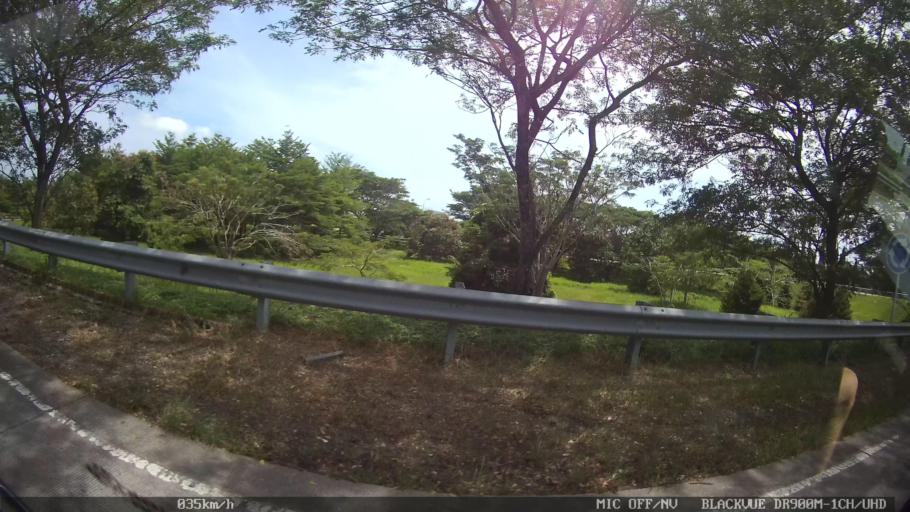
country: ID
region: North Sumatra
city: Percut
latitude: 3.6323
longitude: 98.8768
